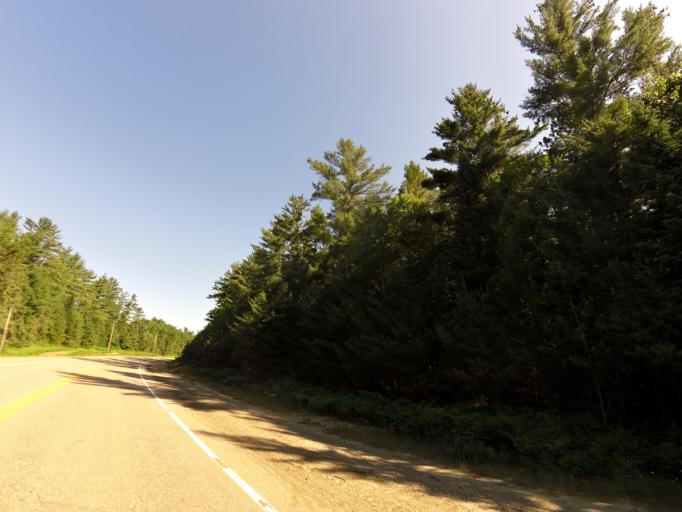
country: CA
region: Ontario
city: Deep River
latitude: 46.1906
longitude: -77.8770
